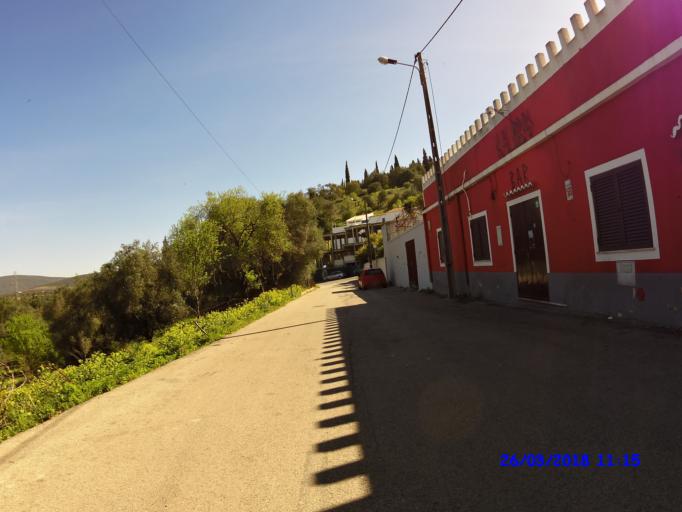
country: PT
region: Faro
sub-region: Loule
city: Boliqueime
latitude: 37.1772
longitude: -8.2022
